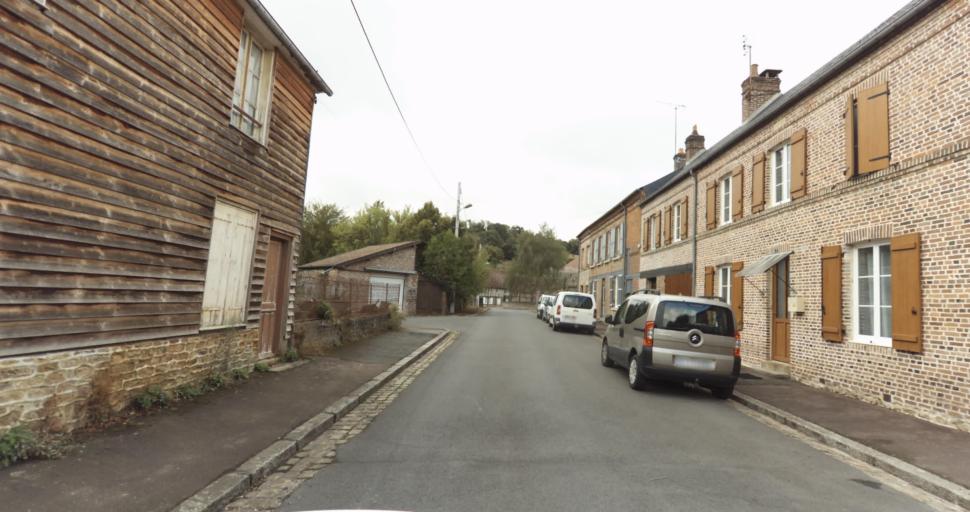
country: FR
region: Lower Normandy
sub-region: Departement de l'Orne
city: Vimoutiers
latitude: 48.9283
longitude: 0.1945
